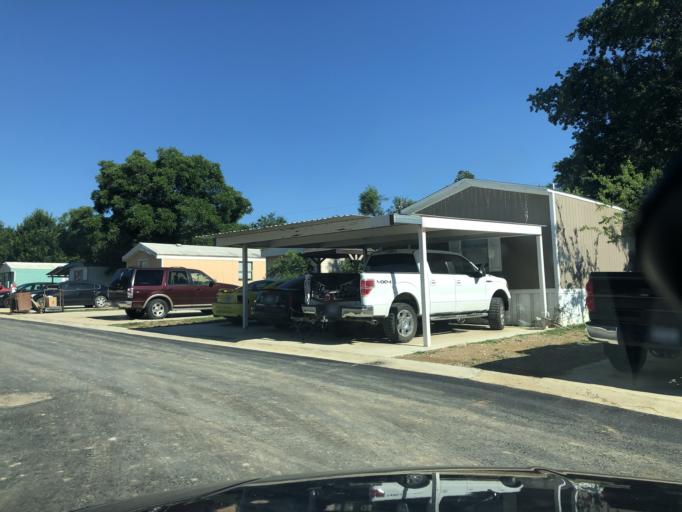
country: US
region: Texas
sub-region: Tarrant County
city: Euless
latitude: 32.8242
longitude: -97.0269
